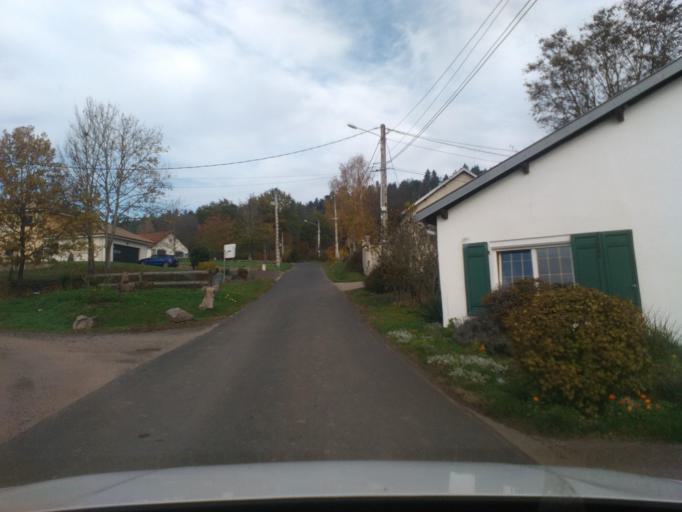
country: FR
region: Lorraine
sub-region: Departement des Vosges
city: Moyenmoutier
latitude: 48.3542
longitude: 6.9304
